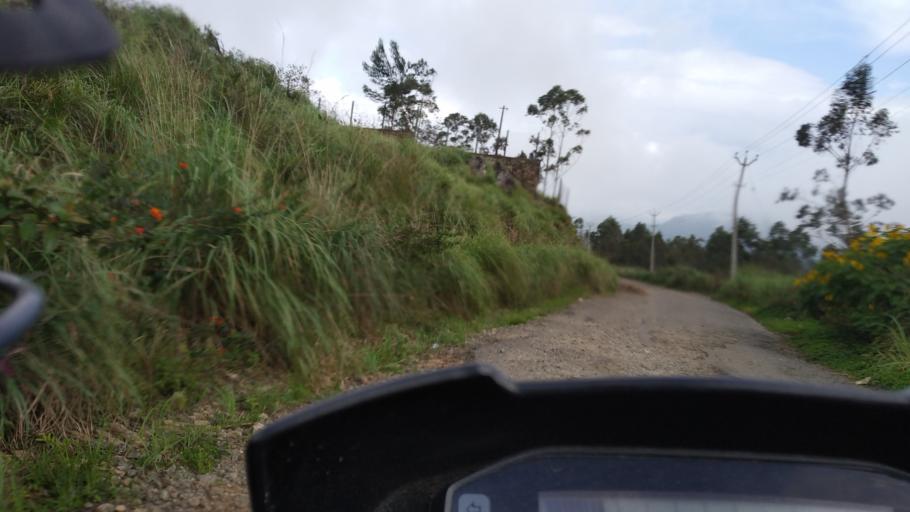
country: IN
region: Kerala
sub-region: Idukki
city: Munnar
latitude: 10.0400
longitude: 77.1803
